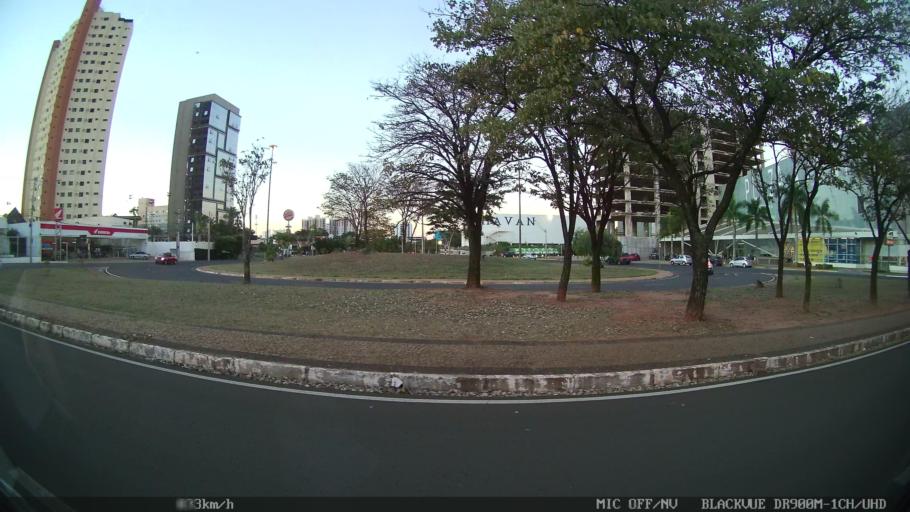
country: BR
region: Sao Paulo
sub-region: Sao Jose Do Rio Preto
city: Sao Jose do Rio Preto
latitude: -20.8270
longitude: -49.3875
